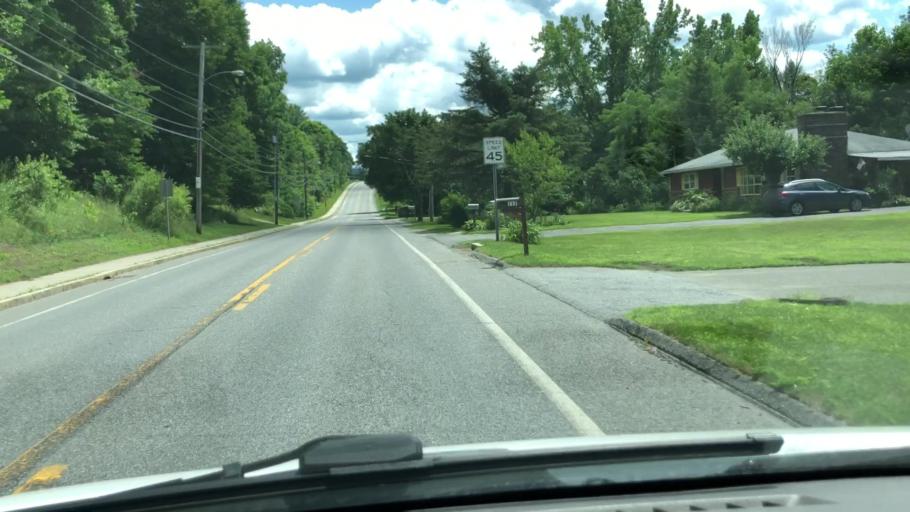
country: US
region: Massachusetts
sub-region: Berkshire County
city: Adams
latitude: 42.6047
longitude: -73.1181
